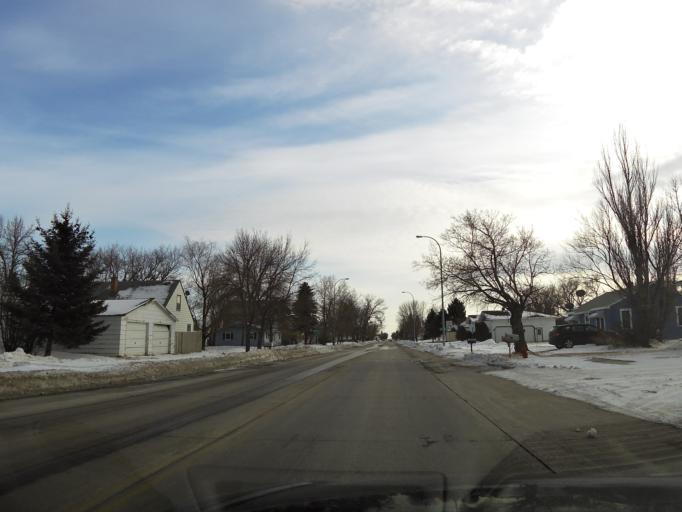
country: US
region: North Dakota
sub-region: Walsh County
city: Grafton
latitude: 48.5668
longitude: -97.1778
